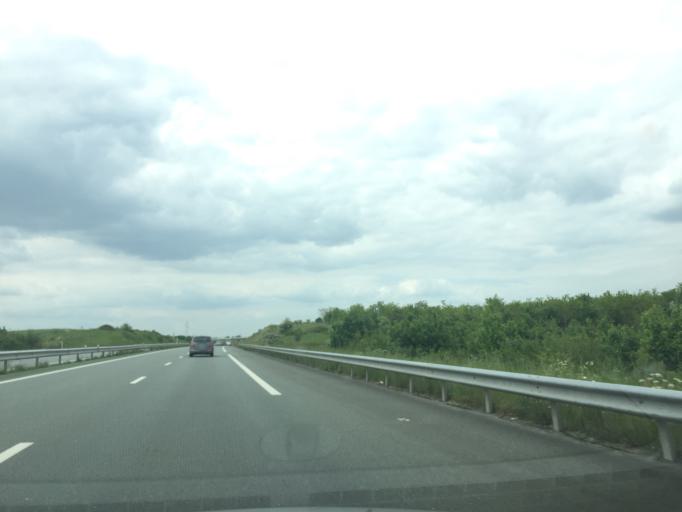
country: FR
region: Poitou-Charentes
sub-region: Departement des Deux-Sevres
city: Saint-Maxire
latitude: 46.4255
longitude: -0.4666
